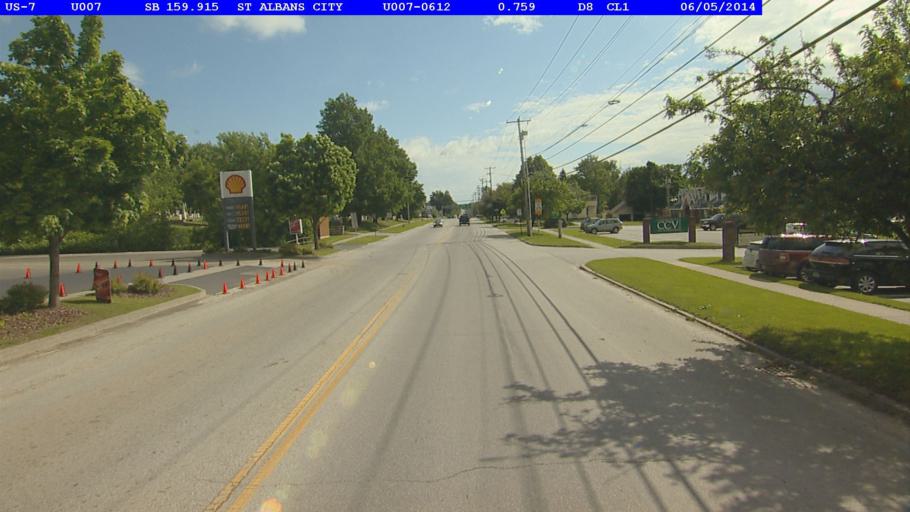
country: US
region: Vermont
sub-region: Franklin County
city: Saint Albans
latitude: 44.8043
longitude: -73.0867
